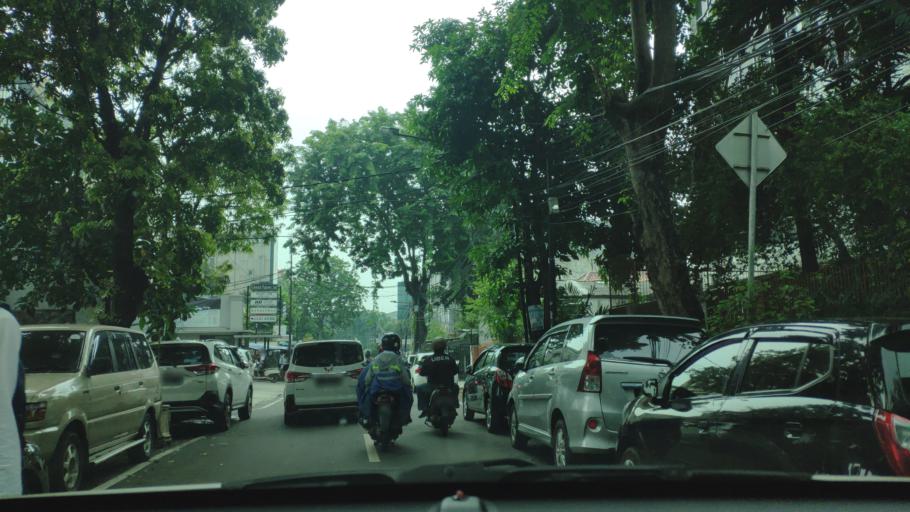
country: ID
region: Jakarta Raya
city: Jakarta
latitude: -6.1687
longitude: 106.8156
